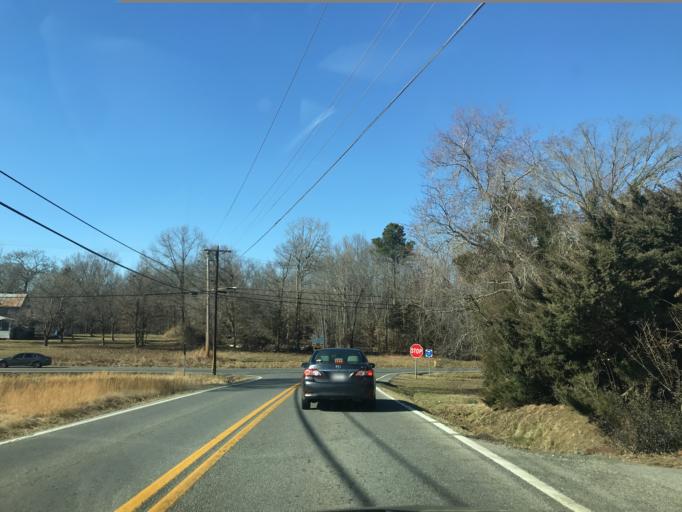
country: US
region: Maryland
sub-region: Charles County
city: Bryans Road
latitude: 38.6078
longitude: -77.0723
